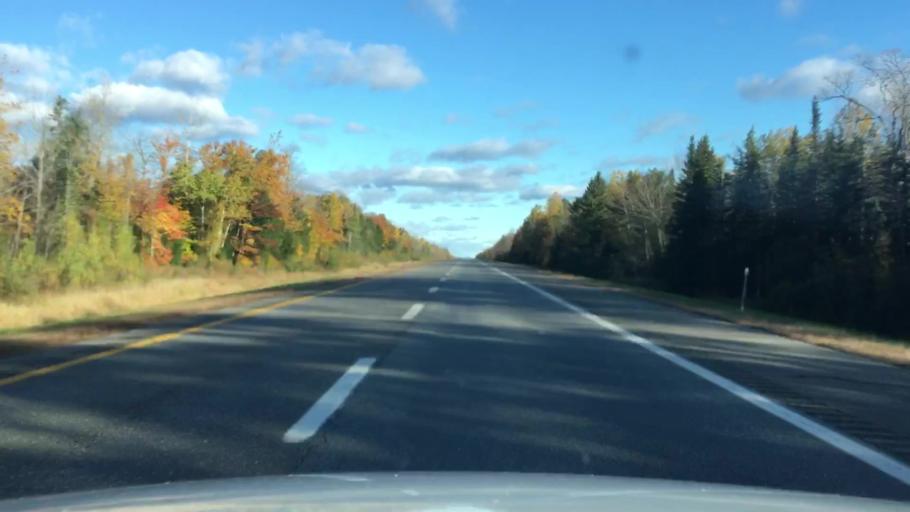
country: US
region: Maine
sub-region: Penobscot County
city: Greenbush
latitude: 45.0760
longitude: -68.6913
